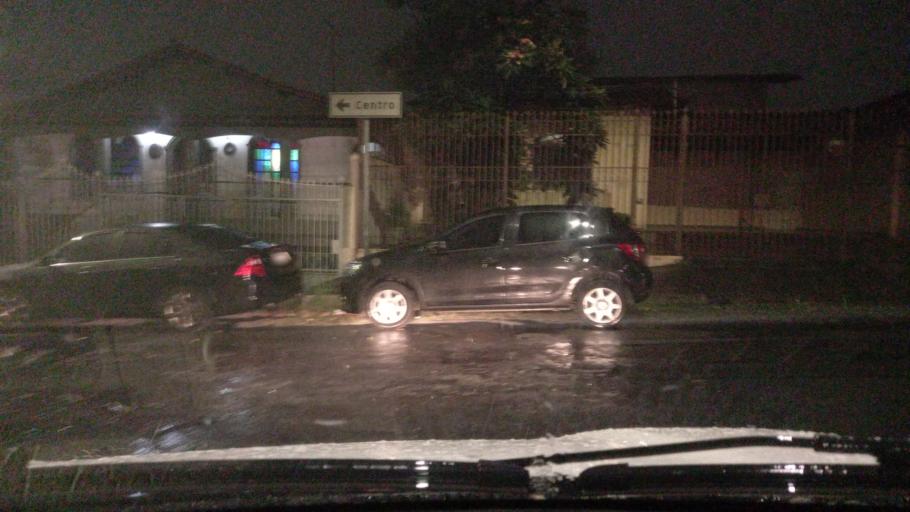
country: BR
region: Minas Gerais
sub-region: Belo Horizonte
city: Belo Horizonte
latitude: -19.9014
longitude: -43.9687
